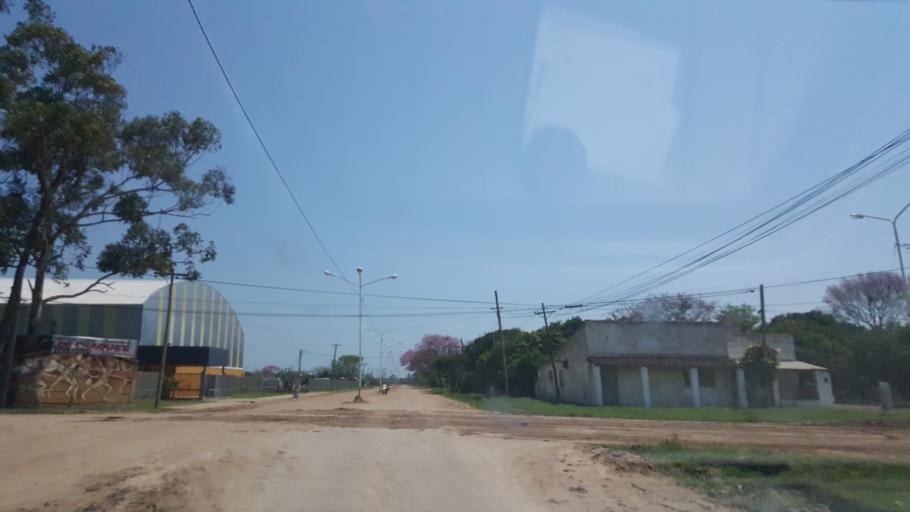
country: AR
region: Corrientes
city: Ita Ibate
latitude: -27.4287
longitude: -57.3421
